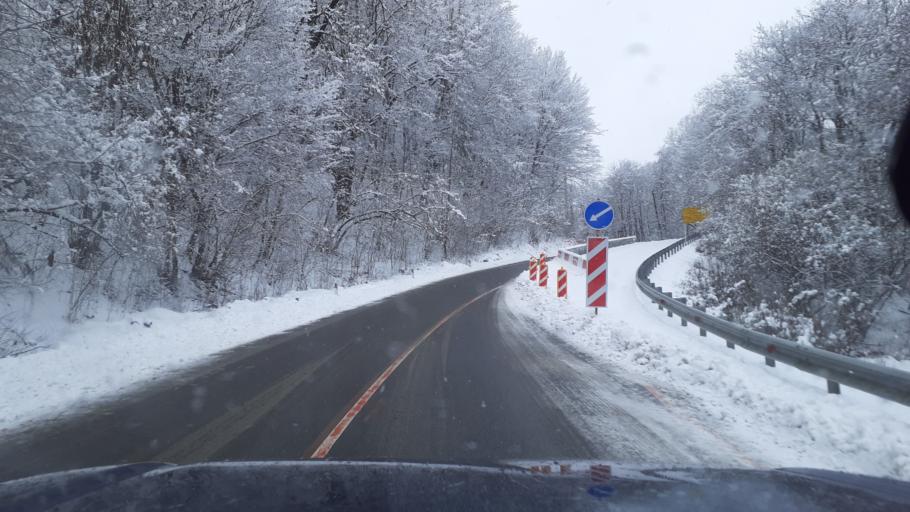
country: RU
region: Adygeya
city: Kamennomostskiy
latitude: 44.1945
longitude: 40.1731
